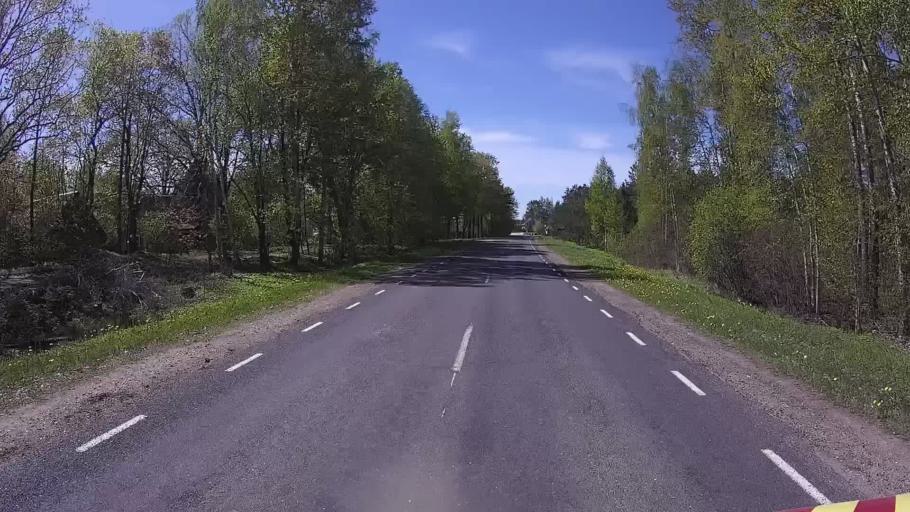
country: EE
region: Polvamaa
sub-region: Raepina vald
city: Rapina
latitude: 58.0116
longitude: 27.3567
